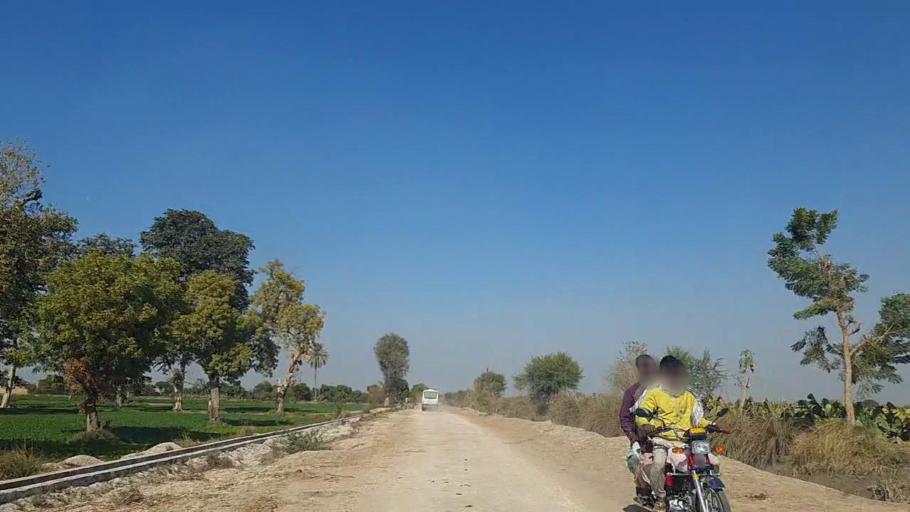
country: PK
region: Sindh
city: Sakrand
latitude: 26.2503
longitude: 68.2207
